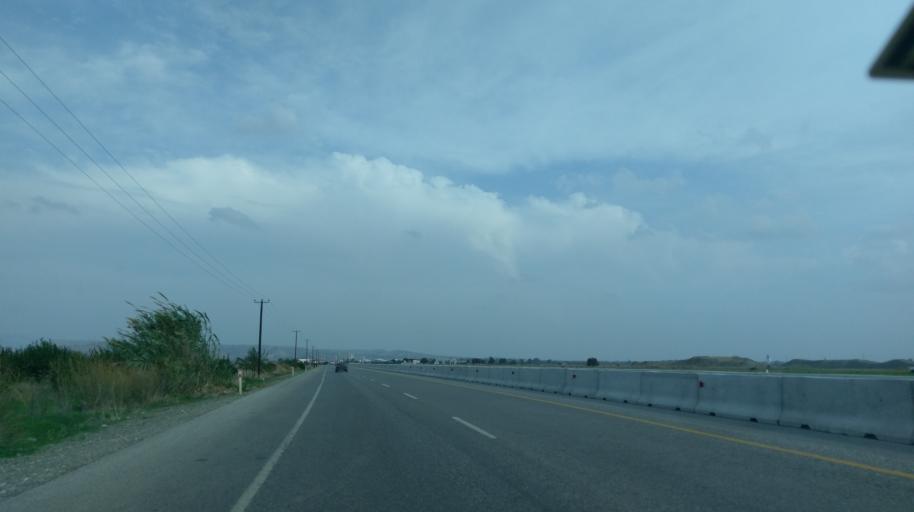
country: CY
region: Lefkosia
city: Morfou
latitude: 35.1985
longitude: 33.0230
